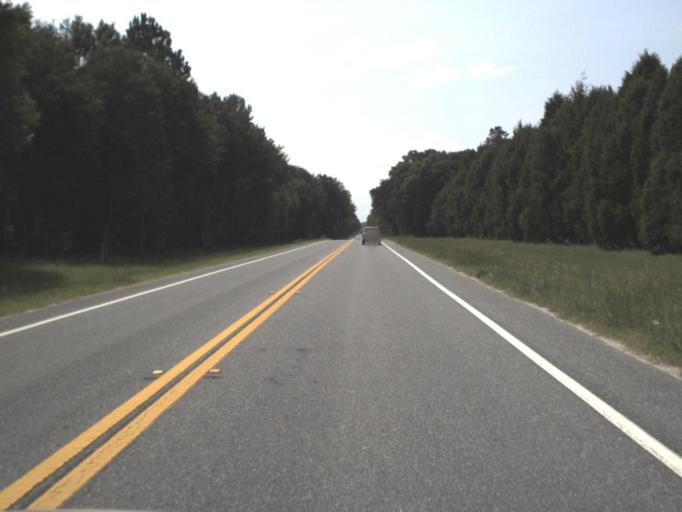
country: US
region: Georgia
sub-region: Echols County
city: Statenville
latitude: 30.5809
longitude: -83.0877
